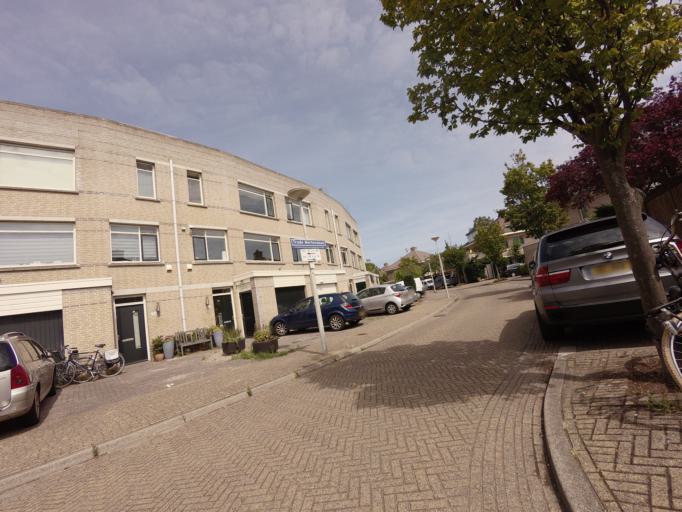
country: NL
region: South Holland
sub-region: Gemeente Den Haag
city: The Hague
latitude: 52.0533
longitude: 4.2657
